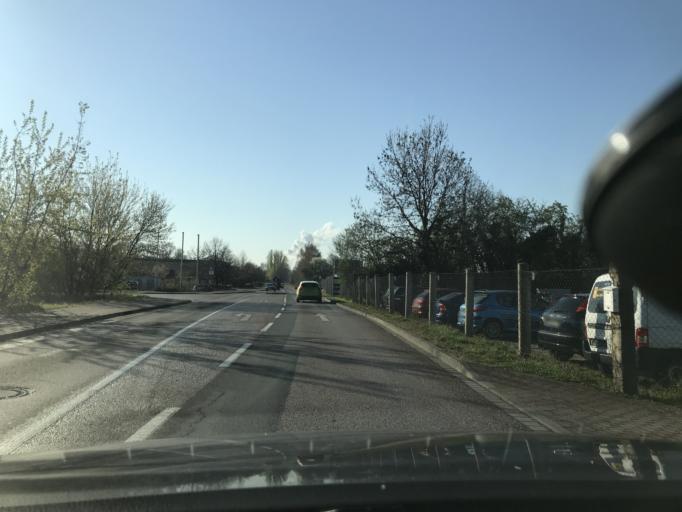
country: DE
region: Saxony-Anhalt
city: Holleben
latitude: 51.4317
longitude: 11.9053
